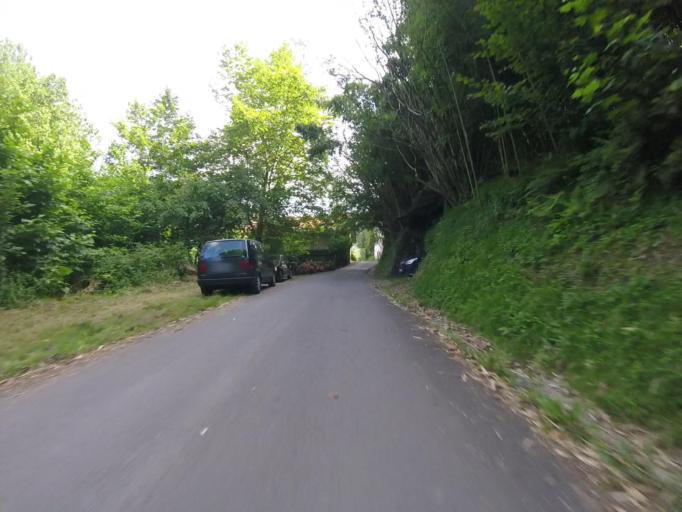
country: ES
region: Basque Country
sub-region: Provincia de Guipuzcoa
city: Astigarraga
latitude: 43.2531
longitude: -1.9502
